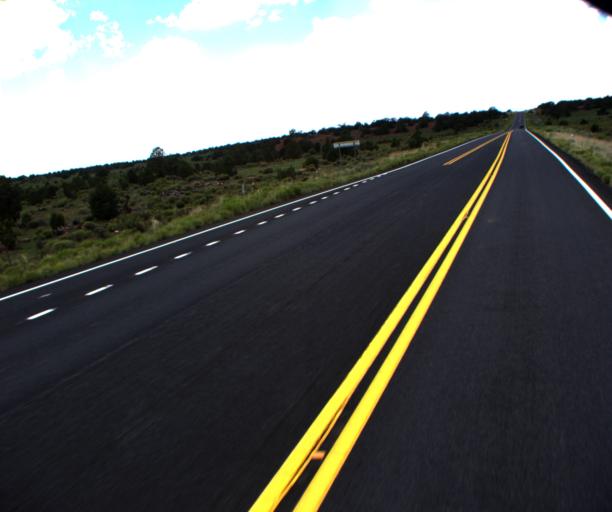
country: US
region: Arizona
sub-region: Coconino County
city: Parks
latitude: 35.6048
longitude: -112.0416
